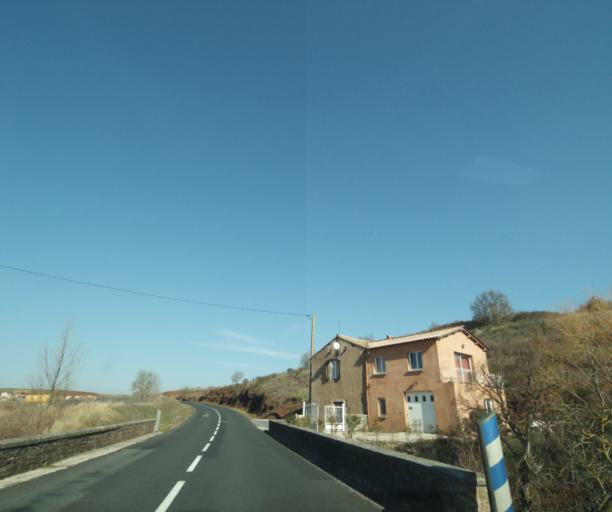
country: FR
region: Midi-Pyrenees
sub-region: Departement de l'Aveyron
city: Camares
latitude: 43.8576
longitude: 2.8304
